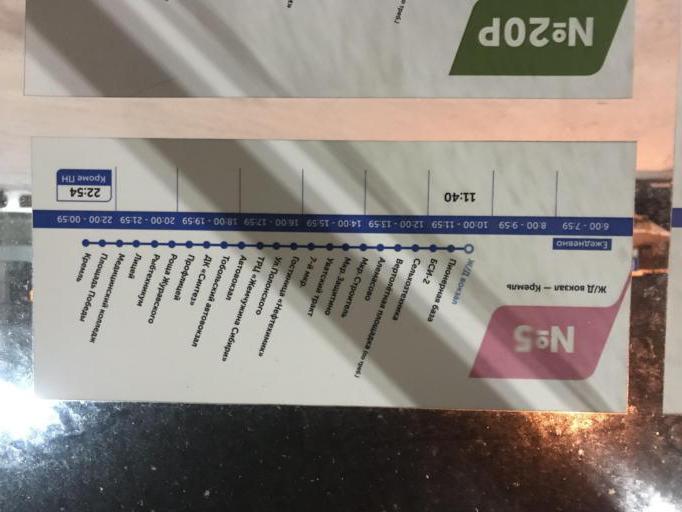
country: RU
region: Tjumen
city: Tobol'sk
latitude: 58.2879
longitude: 68.3109
